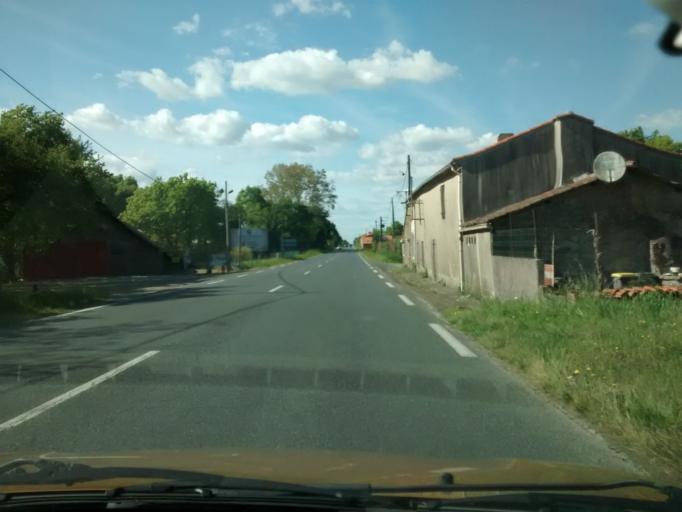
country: FR
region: Pays de la Loire
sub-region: Departement de la Loire-Atlantique
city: Geneston
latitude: 47.0715
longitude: -1.5204
